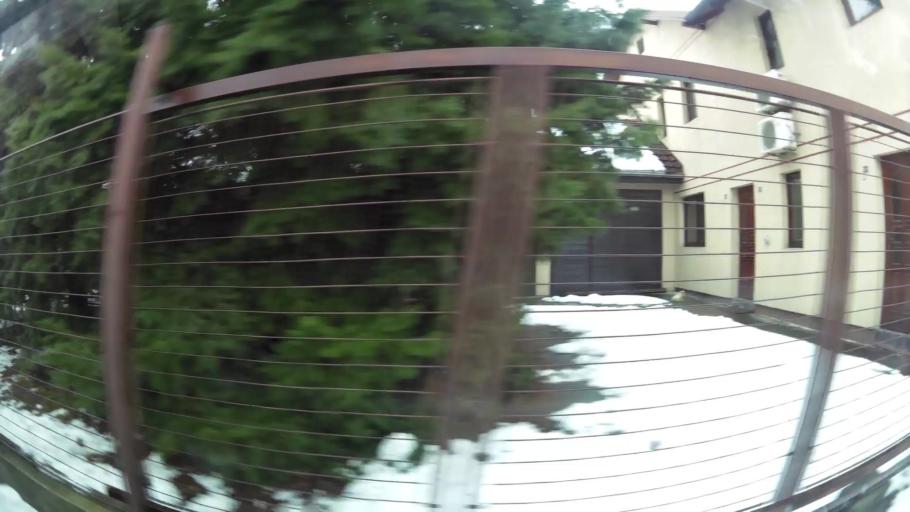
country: RS
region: Central Serbia
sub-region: Belgrade
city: Zemun
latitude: 44.8443
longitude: 20.3618
